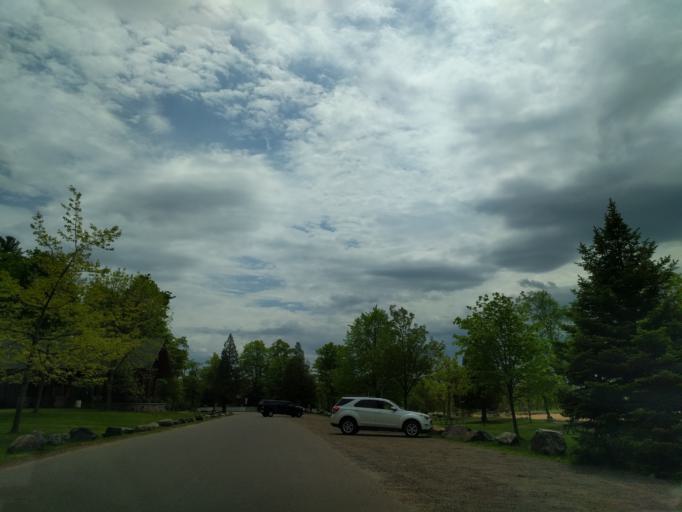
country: US
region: Michigan
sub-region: Marquette County
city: Marquette
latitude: 46.5871
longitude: -87.3853
